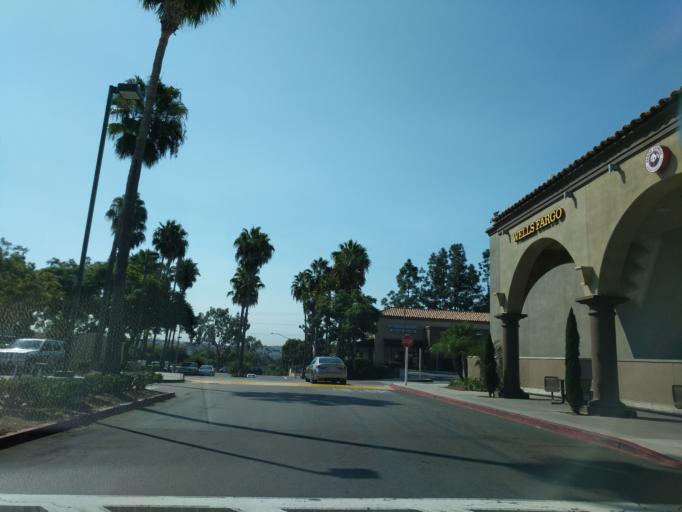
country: US
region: California
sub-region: San Diego County
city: Lake San Marcos
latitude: 33.1034
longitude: -117.2682
